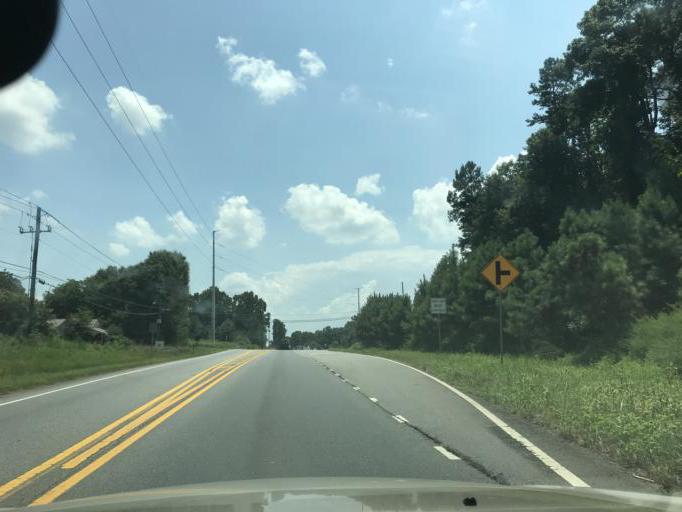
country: US
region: Georgia
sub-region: Forsyth County
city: Cumming
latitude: 34.2847
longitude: -84.1263
